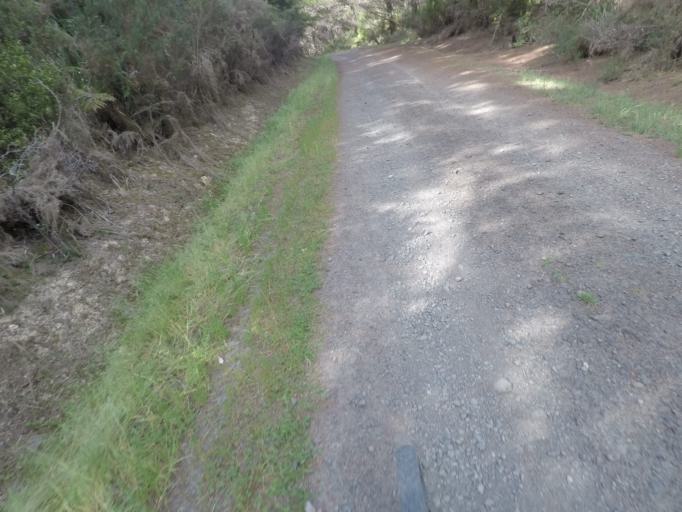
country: NZ
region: Auckland
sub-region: Auckland
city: Muriwai Beach
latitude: -36.7417
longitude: 174.5716
